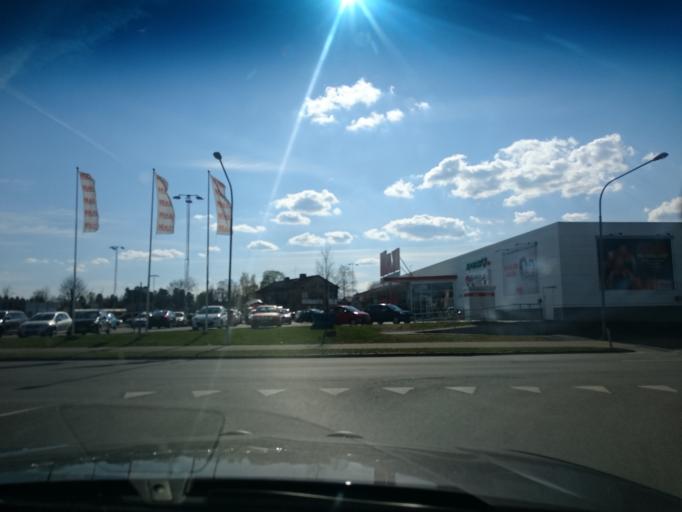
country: SE
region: Joenkoeping
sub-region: Vetlanda Kommun
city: Vetlanda
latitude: 57.4256
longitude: 15.0976
